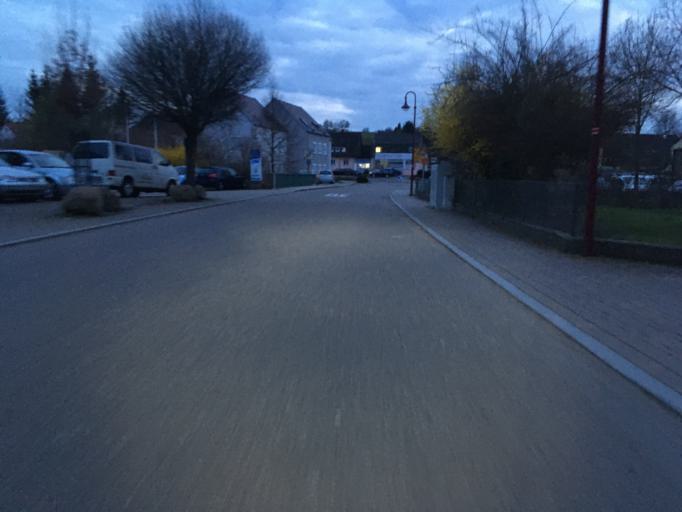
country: DE
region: Baden-Wuerttemberg
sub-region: Regierungsbezirk Stuttgart
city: Lowenstein
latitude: 49.1336
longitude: 9.3831
